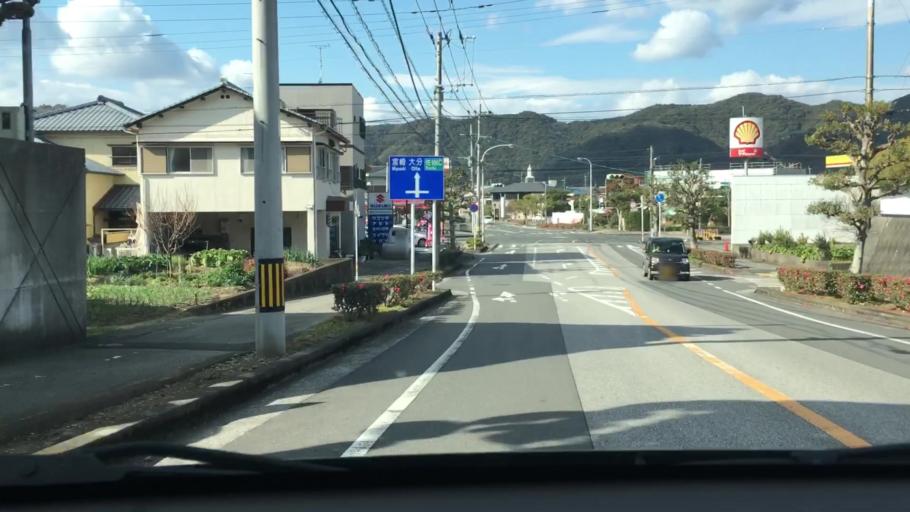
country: JP
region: Oita
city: Saiki
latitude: 32.9580
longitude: 131.9059
